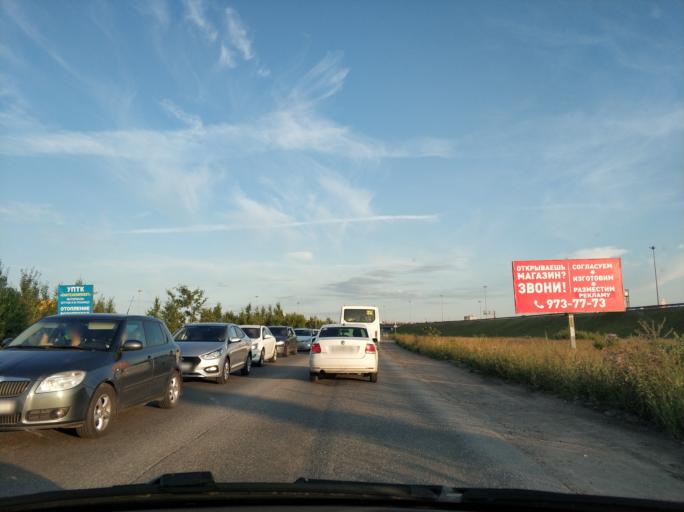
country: RU
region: Leningrad
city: Bugry
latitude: 60.0625
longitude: 30.3889
